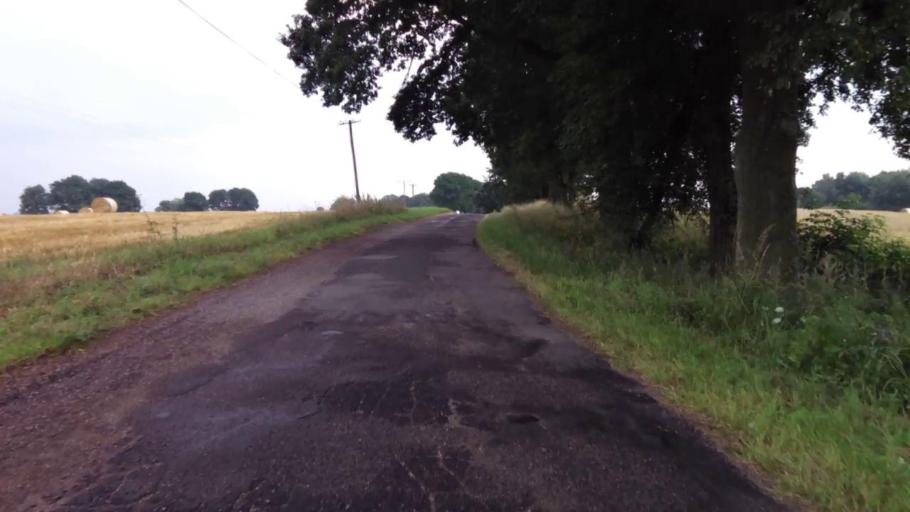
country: PL
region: West Pomeranian Voivodeship
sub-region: Powiat drawski
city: Drawsko Pomorskie
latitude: 53.5357
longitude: 15.7355
